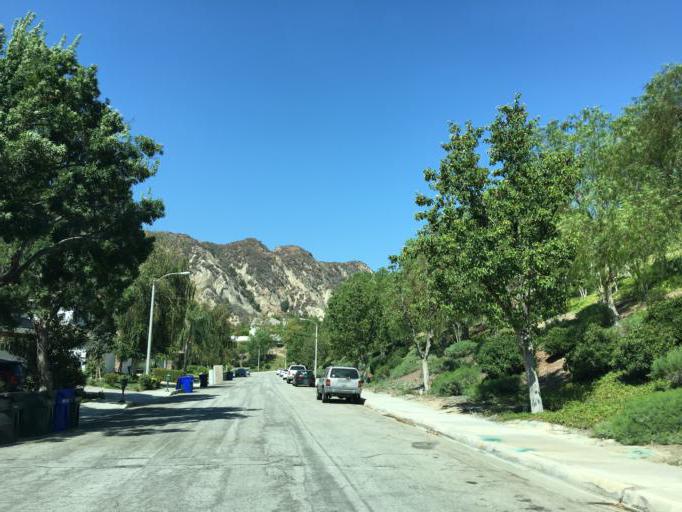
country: US
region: California
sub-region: Los Angeles County
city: Santa Clarita
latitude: 34.3836
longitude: -118.5875
